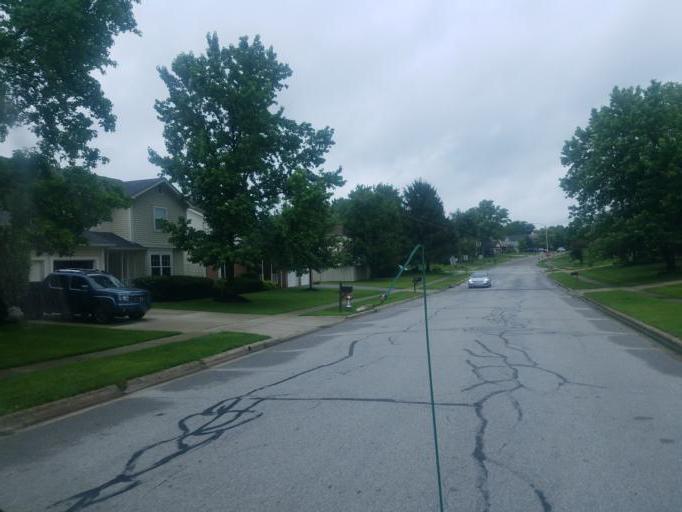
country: US
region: Ohio
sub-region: Franklin County
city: Gahanna
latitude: 40.0124
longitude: -82.8516
